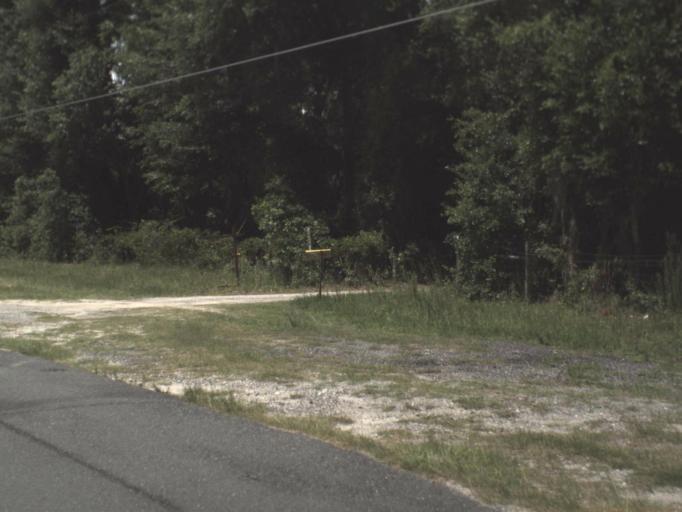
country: US
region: Florida
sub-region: Alachua County
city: Hawthorne
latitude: 29.6329
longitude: -82.0303
